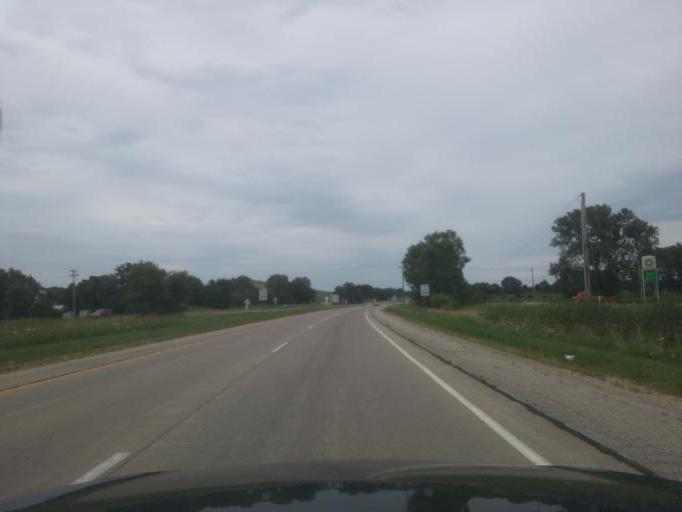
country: US
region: Wisconsin
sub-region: Dane County
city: McFarland
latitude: 43.0453
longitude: -89.2683
